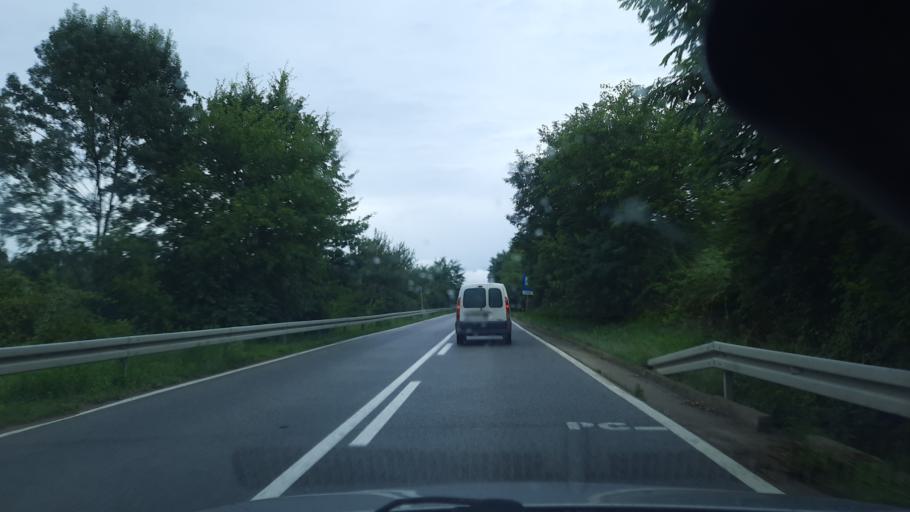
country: RS
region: Central Serbia
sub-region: Raski Okrug
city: Kraljevo
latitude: 43.7628
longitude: 20.8057
